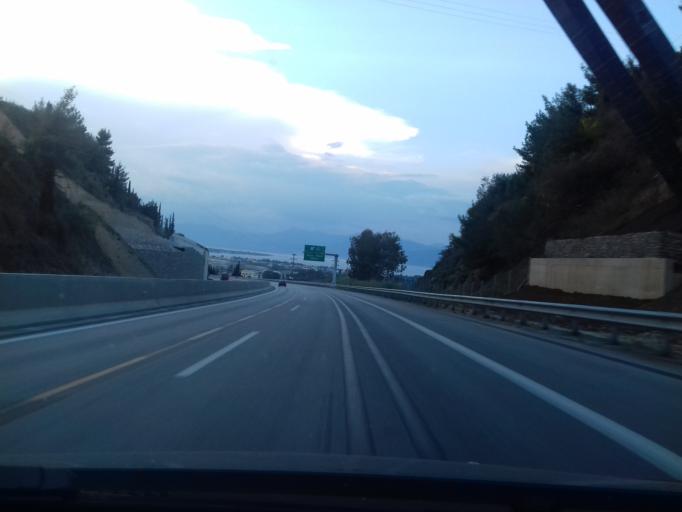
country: GR
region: West Greece
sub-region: Nomos Achaias
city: Aigio
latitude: 38.2525
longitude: 22.0698
